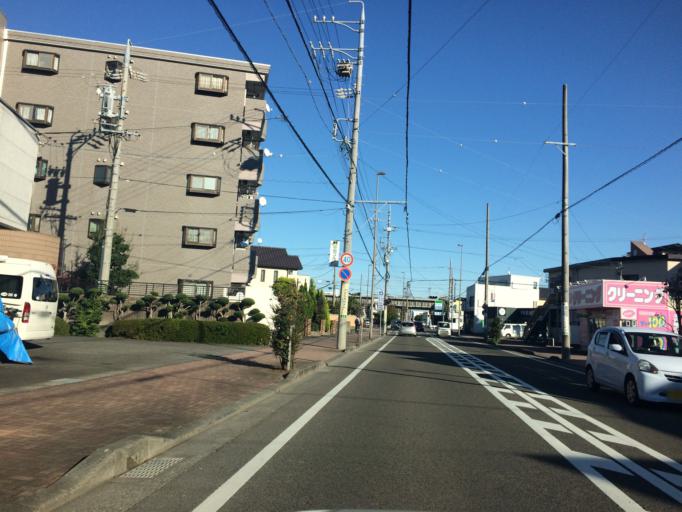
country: JP
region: Shizuoka
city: Shizuoka-shi
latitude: 34.9441
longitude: 138.3612
